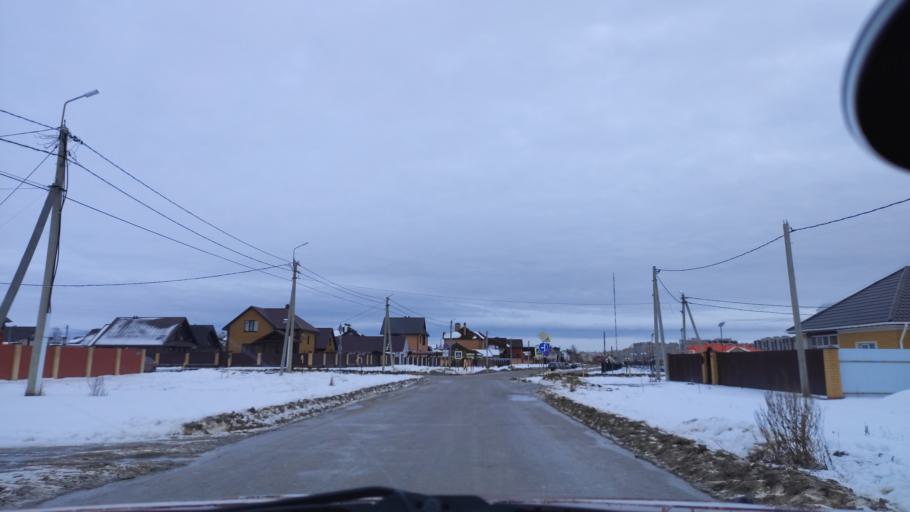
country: RU
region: Tambov
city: Tambov
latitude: 52.7699
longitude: 41.3779
